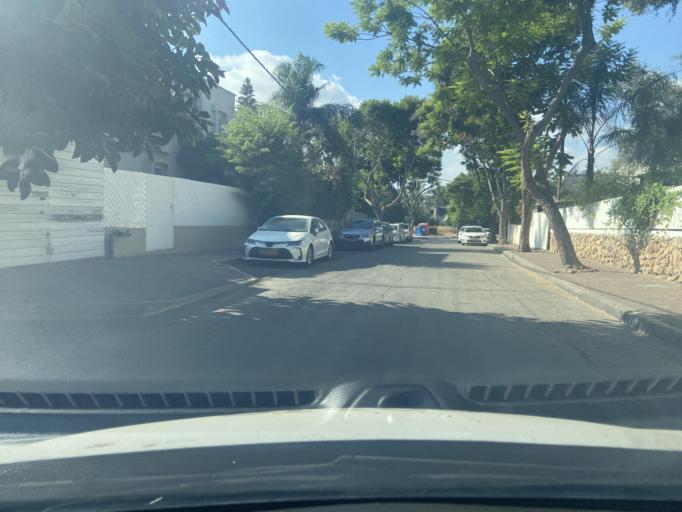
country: IL
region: Central District
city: Yehud
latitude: 32.0373
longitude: 34.8952
